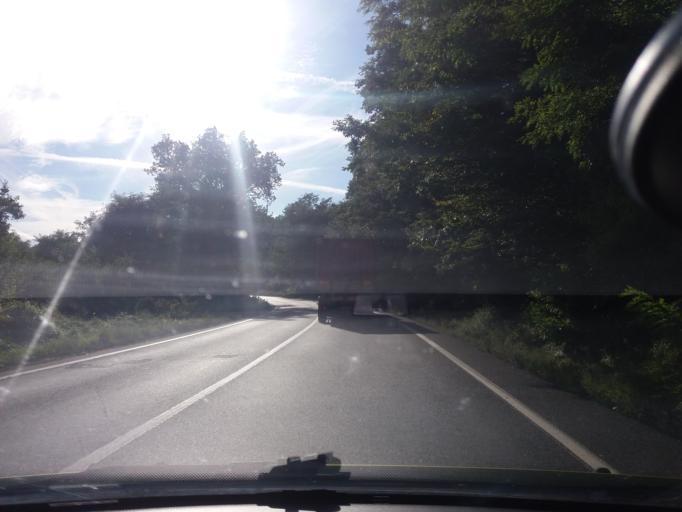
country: RO
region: Arad
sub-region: Comuna Ususau
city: Ususau
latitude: 46.1084
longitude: 21.7686
